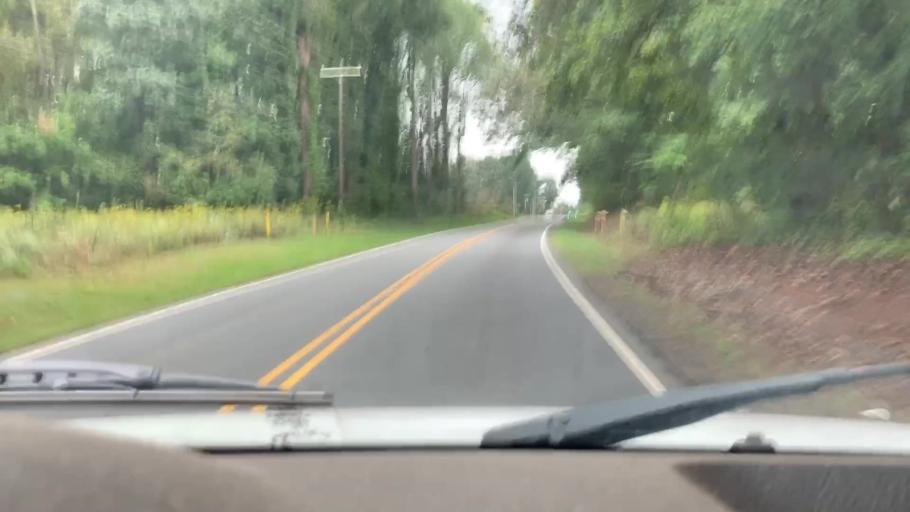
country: US
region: North Carolina
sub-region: Mecklenburg County
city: Huntersville
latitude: 35.3609
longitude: -80.8235
